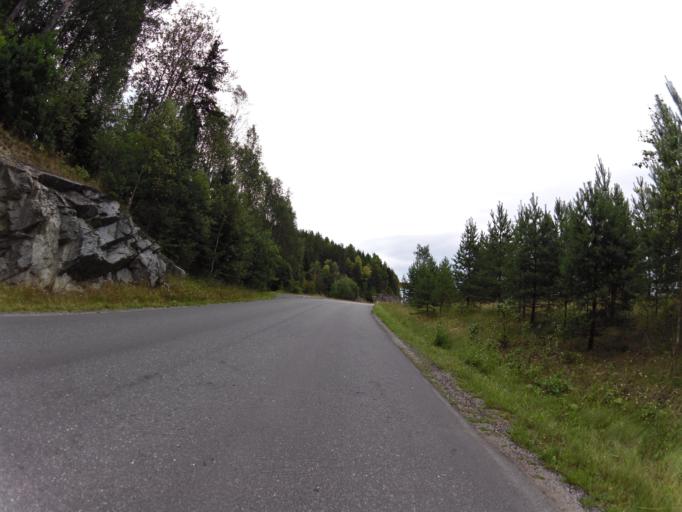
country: NO
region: Akershus
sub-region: As
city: As
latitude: 59.6902
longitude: 10.7354
